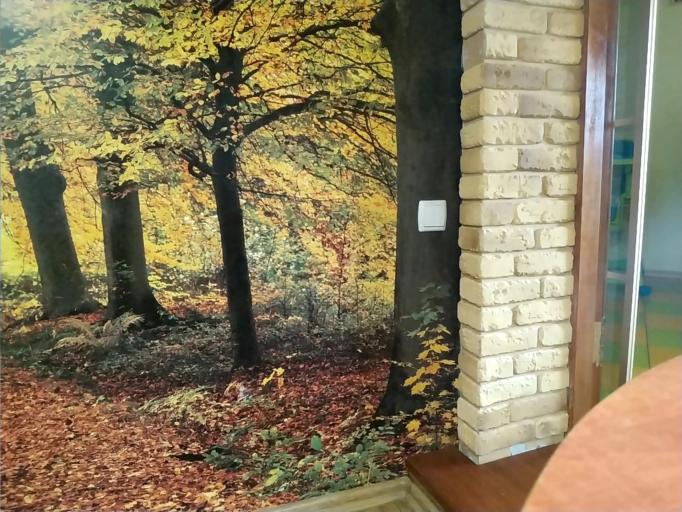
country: RU
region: Smolensk
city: Dorogobuzh
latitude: 54.8621
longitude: 33.3144
